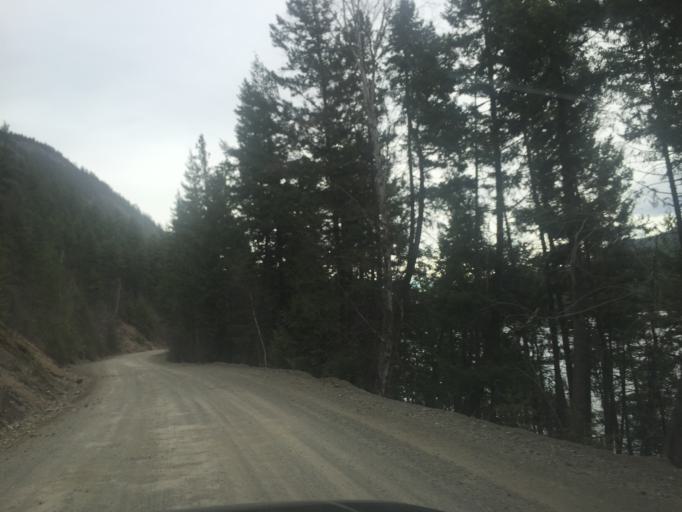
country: CA
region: British Columbia
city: Chase
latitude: 51.4224
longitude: -120.1336
